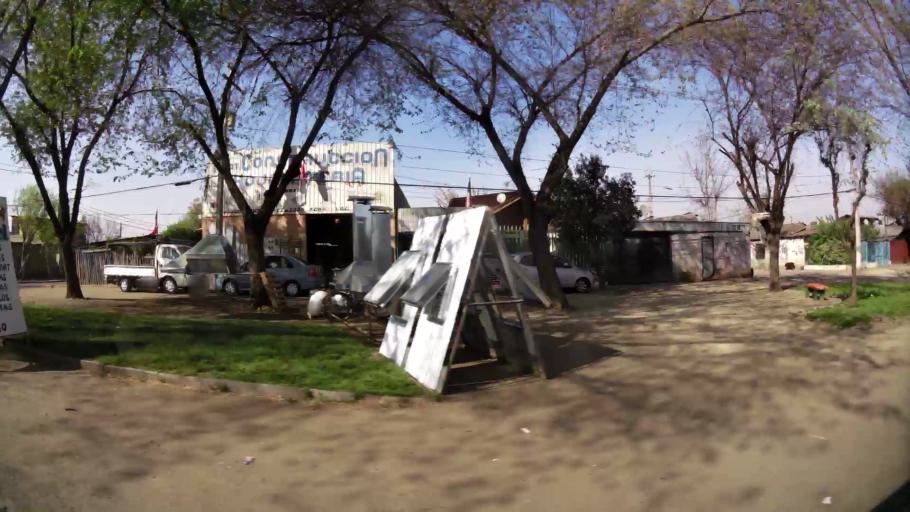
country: CL
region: Santiago Metropolitan
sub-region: Provincia de Santiago
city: Lo Prado
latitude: -33.4185
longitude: -70.7389
